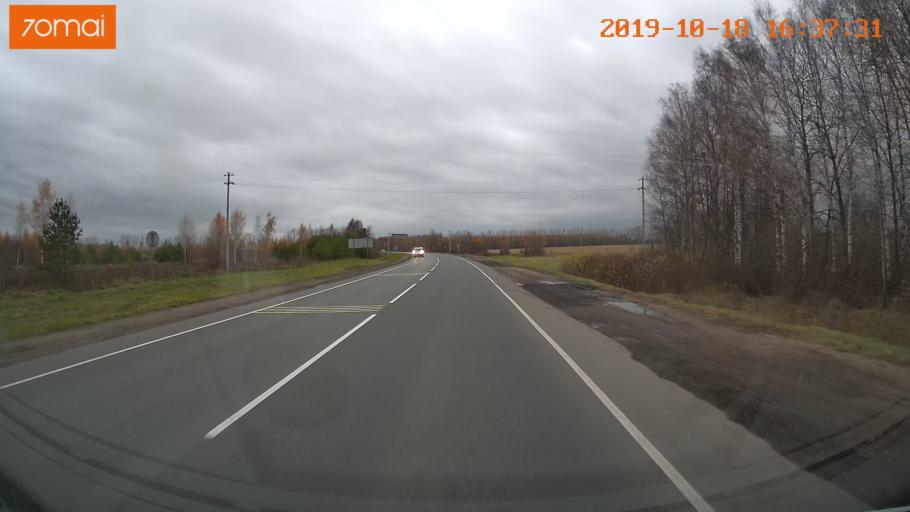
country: RU
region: Vladimir
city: Suzdal'
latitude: 56.4231
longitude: 40.4768
